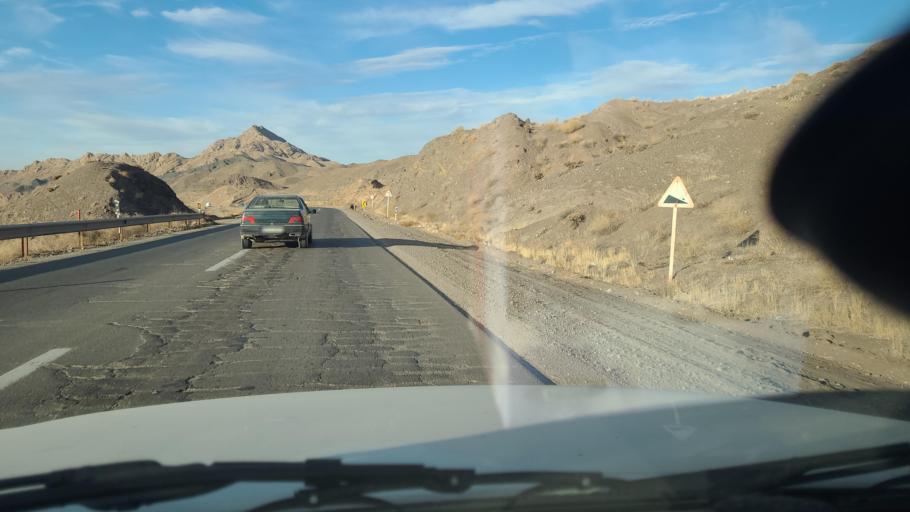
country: IR
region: Razavi Khorasan
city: Sabzevar
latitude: 36.4287
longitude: 57.5629
